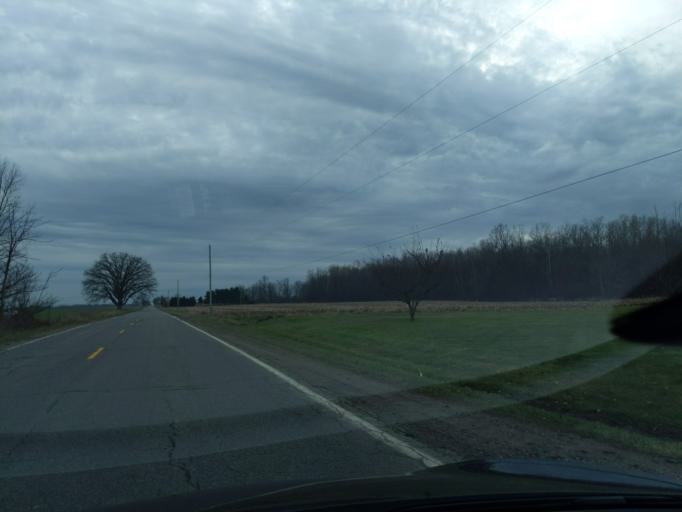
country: US
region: Michigan
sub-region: Ingham County
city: Williamston
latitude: 42.6661
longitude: -84.3637
